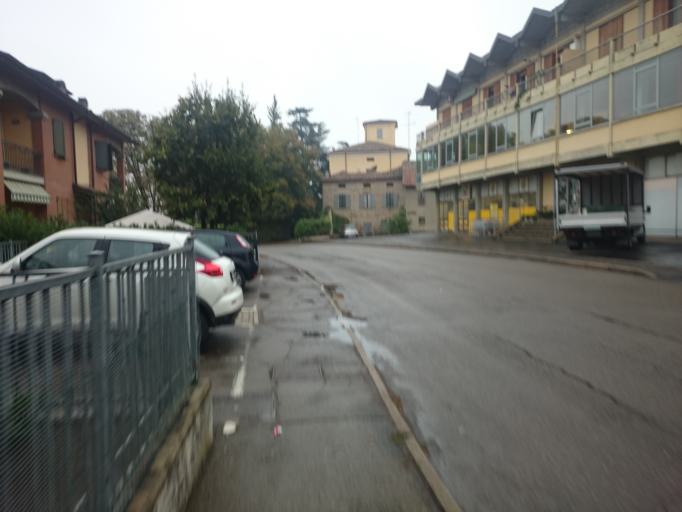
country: IT
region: Emilia-Romagna
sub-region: Provincia di Reggio Emilia
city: Scandiano
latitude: 44.5978
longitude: 10.6988
